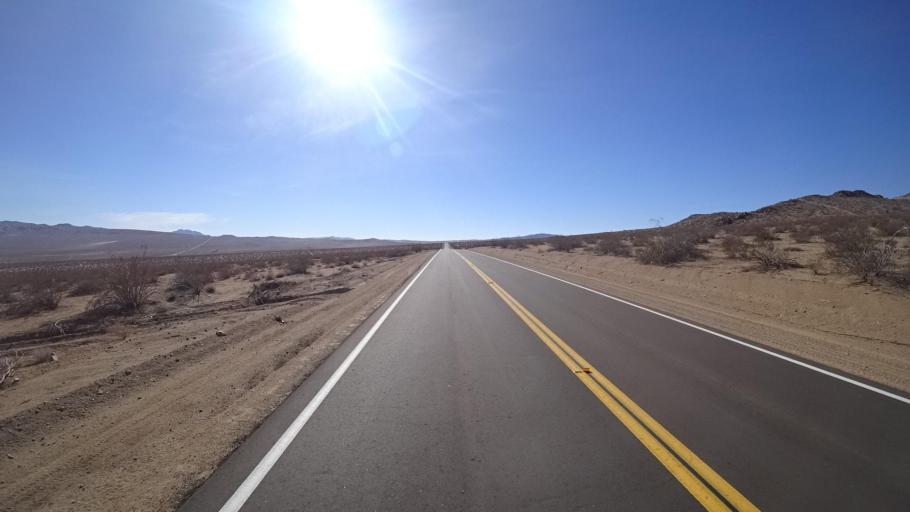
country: US
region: California
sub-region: Kern County
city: Ridgecrest
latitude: 35.5386
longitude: -117.5856
